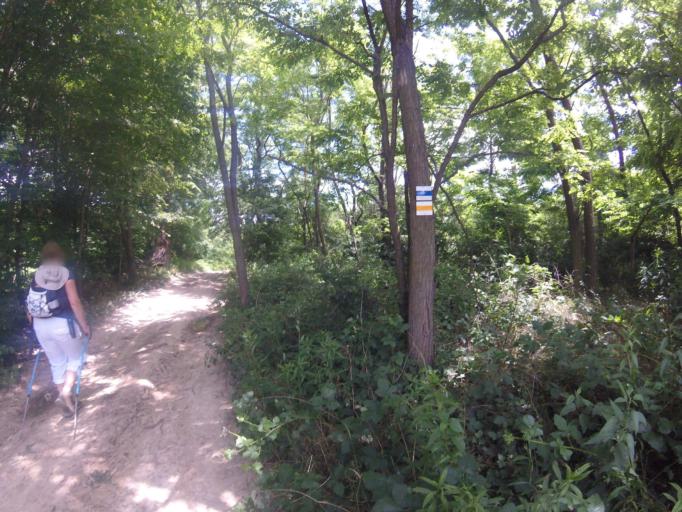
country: HU
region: Zala
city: Zalalovo
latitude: 46.8264
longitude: 16.5566
